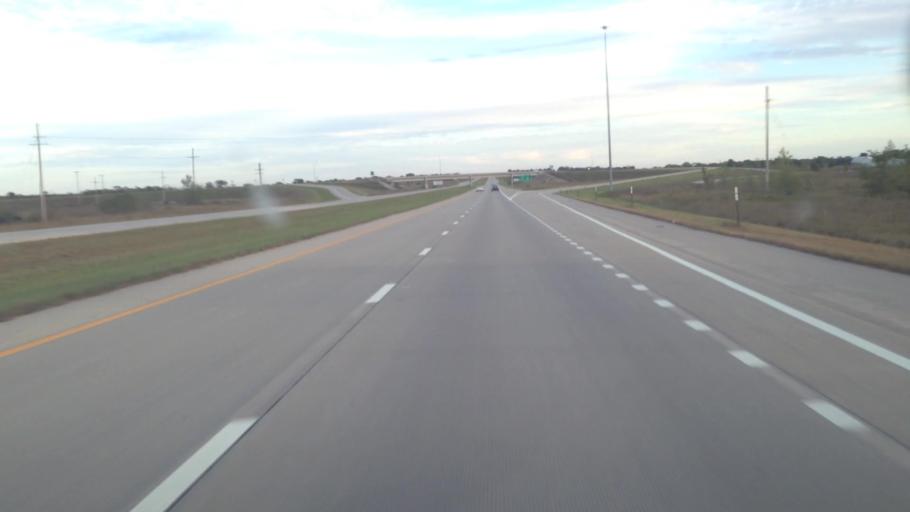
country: US
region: Kansas
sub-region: Franklin County
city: Ottawa
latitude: 38.6685
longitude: -95.2544
